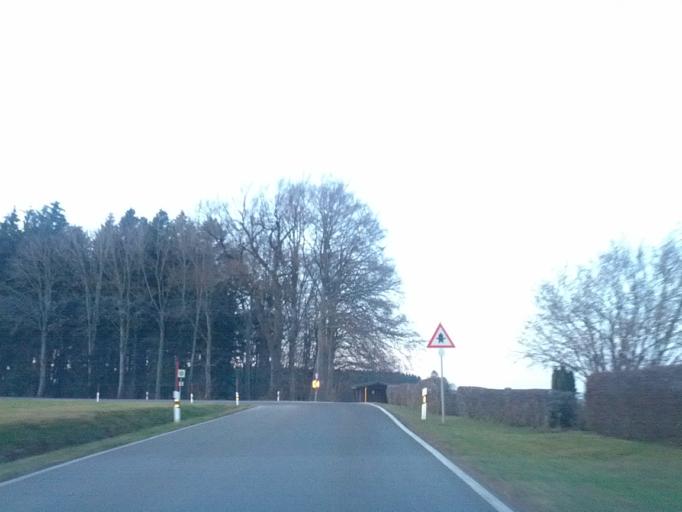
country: DE
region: Baden-Wuerttemberg
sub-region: Tuebingen Region
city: Aitrach
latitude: 47.9369
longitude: 10.0450
